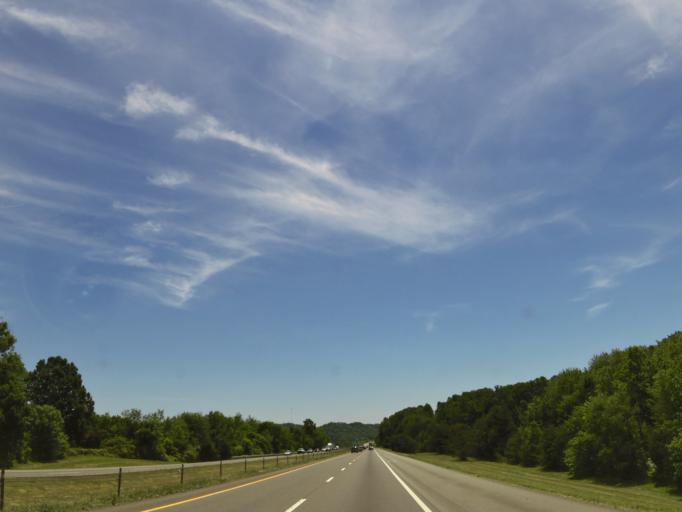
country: US
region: Tennessee
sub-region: Knox County
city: Knoxville
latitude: 36.0600
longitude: -84.0071
